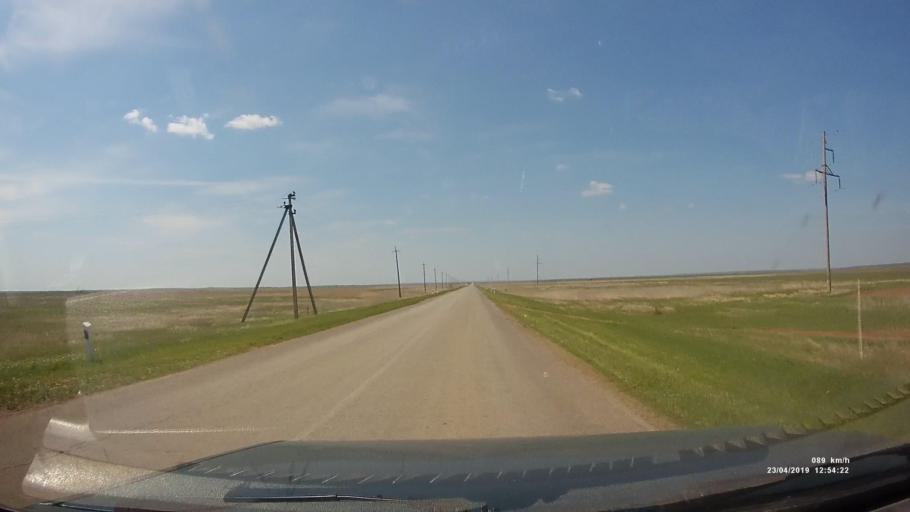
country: RU
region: Kalmykiya
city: Yashalta
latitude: 46.5797
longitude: 42.5796
